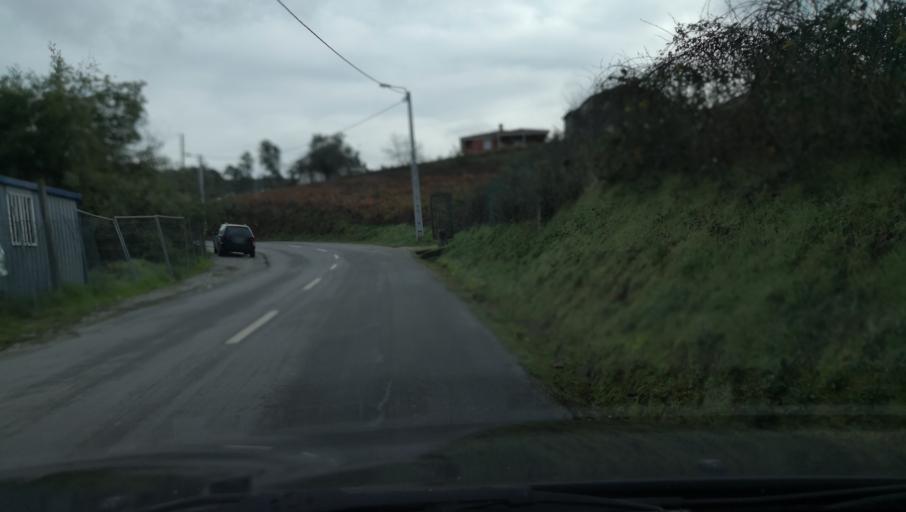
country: PT
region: Vila Real
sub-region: Vila Real
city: Vila Real
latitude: 41.2885
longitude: -7.7147
